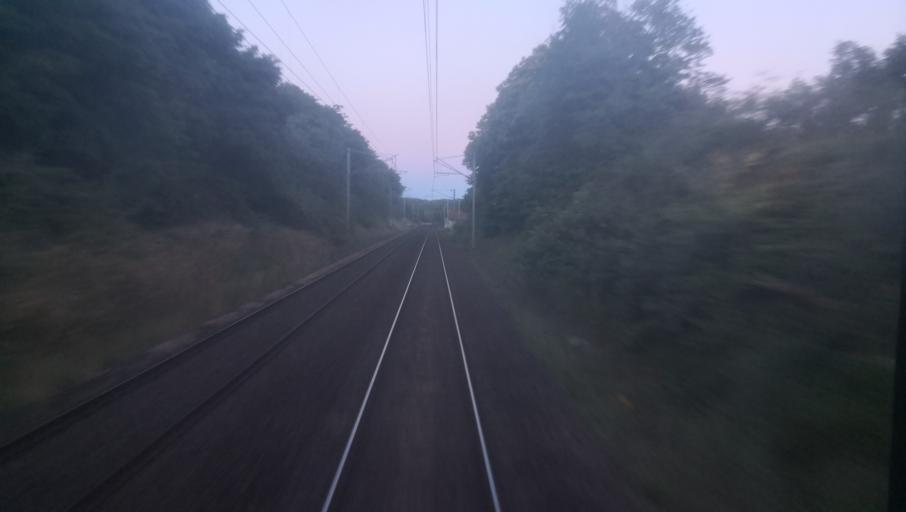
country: FR
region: Centre
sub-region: Departement du Loiret
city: Saint-Brisson-sur-Loire
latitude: 47.6696
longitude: 2.6941
